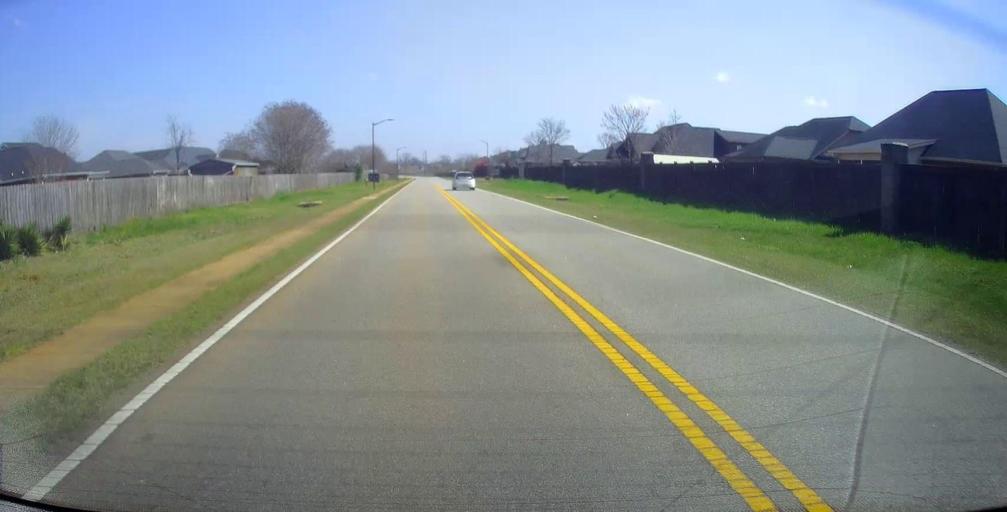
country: US
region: Georgia
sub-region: Houston County
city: Centerville
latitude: 32.5672
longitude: -83.7151
